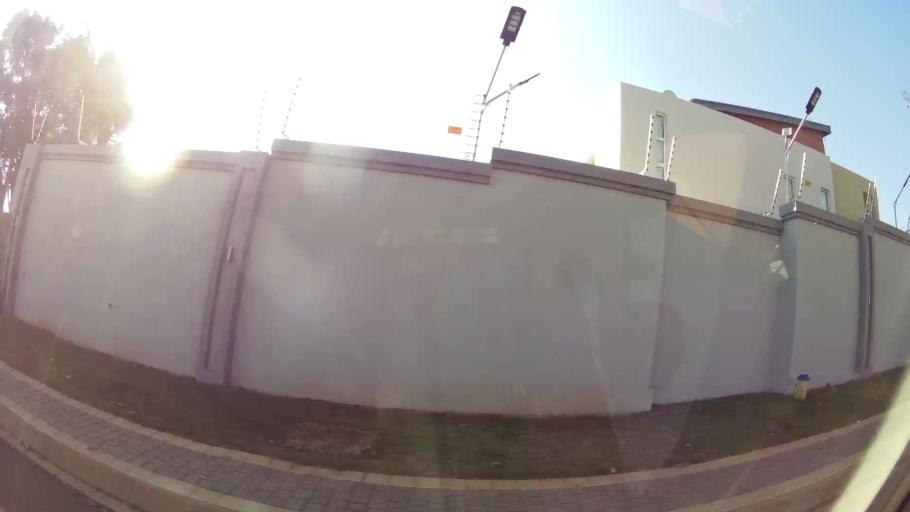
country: ZA
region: Gauteng
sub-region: Ekurhuleni Metropolitan Municipality
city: Germiston
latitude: -26.1725
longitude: 28.1537
